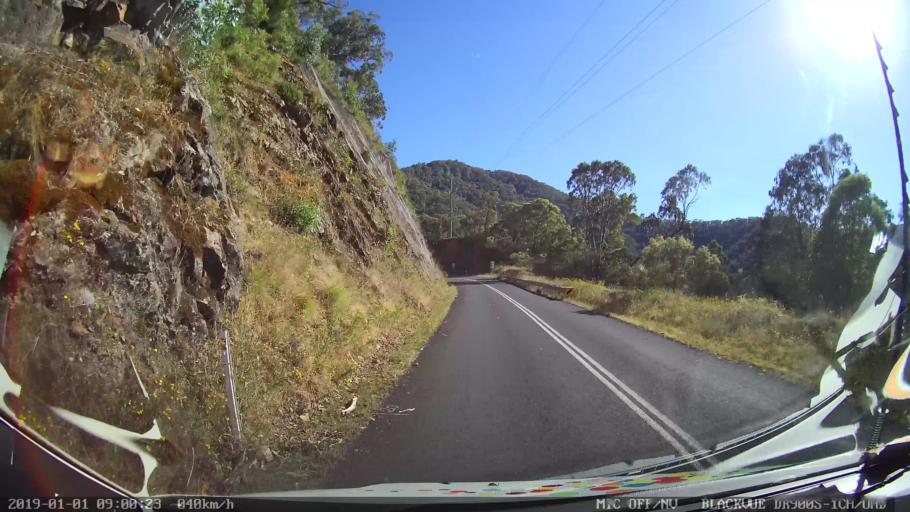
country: AU
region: New South Wales
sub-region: Snowy River
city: Jindabyne
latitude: -36.2356
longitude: 148.1821
